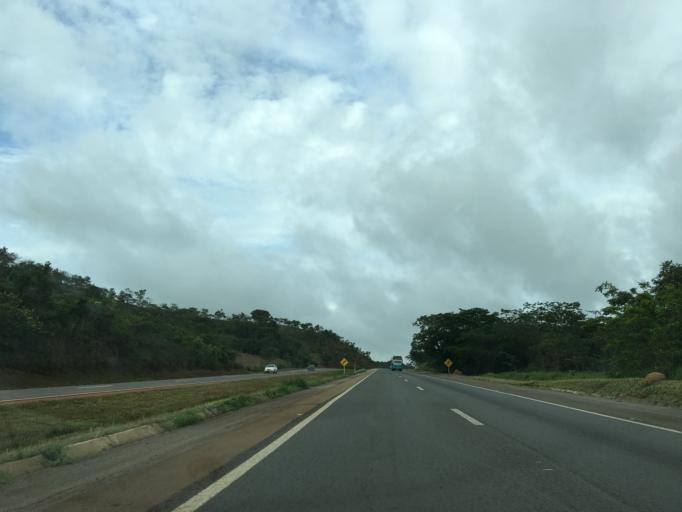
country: BR
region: Goias
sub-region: Luziania
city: Luziania
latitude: -16.1109
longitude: -48.3033
